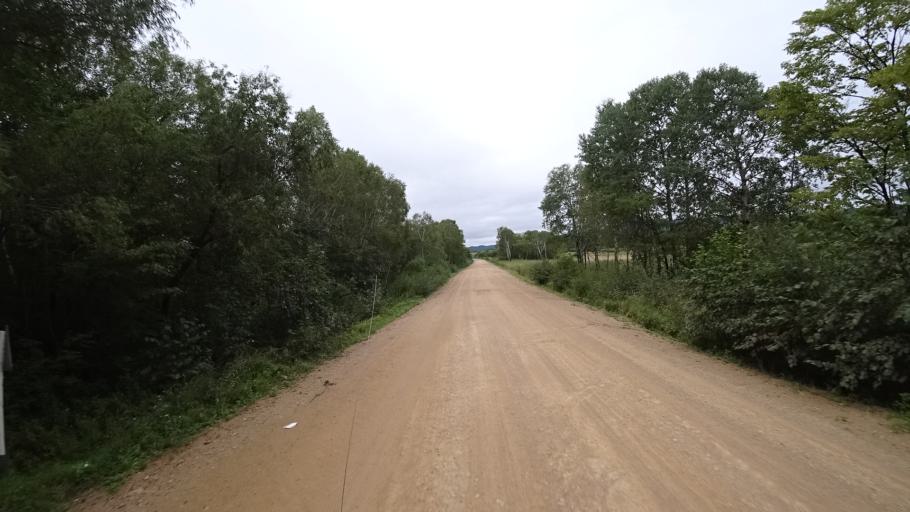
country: RU
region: Primorskiy
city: Rettikhovka
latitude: 44.1618
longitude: 132.7257
